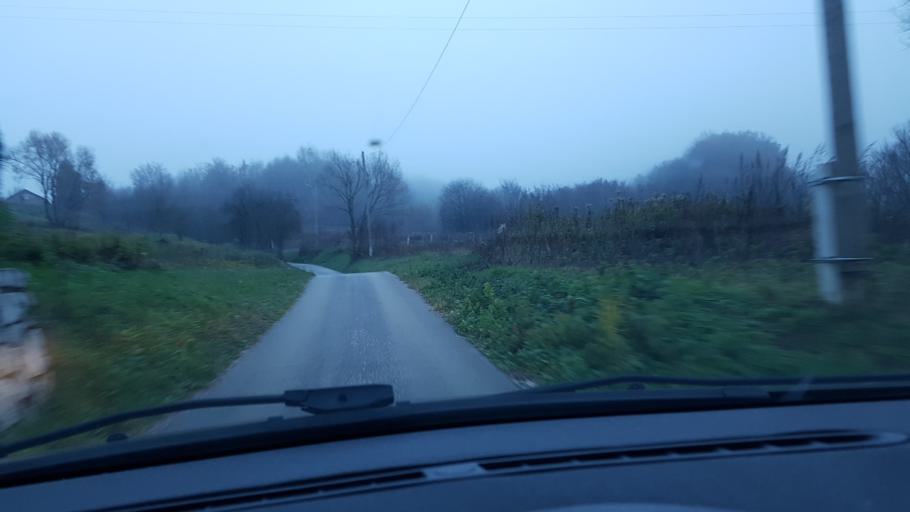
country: HR
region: Krapinsko-Zagorska
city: Pregrada
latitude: 46.2060
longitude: 15.7870
